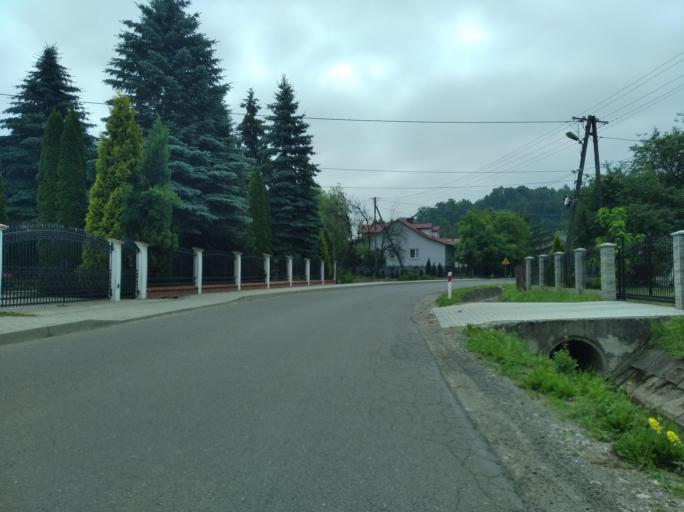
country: PL
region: Subcarpathian Voivodeship
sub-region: Powiat sanocki
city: Besko
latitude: 49.5896
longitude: 21.9458
